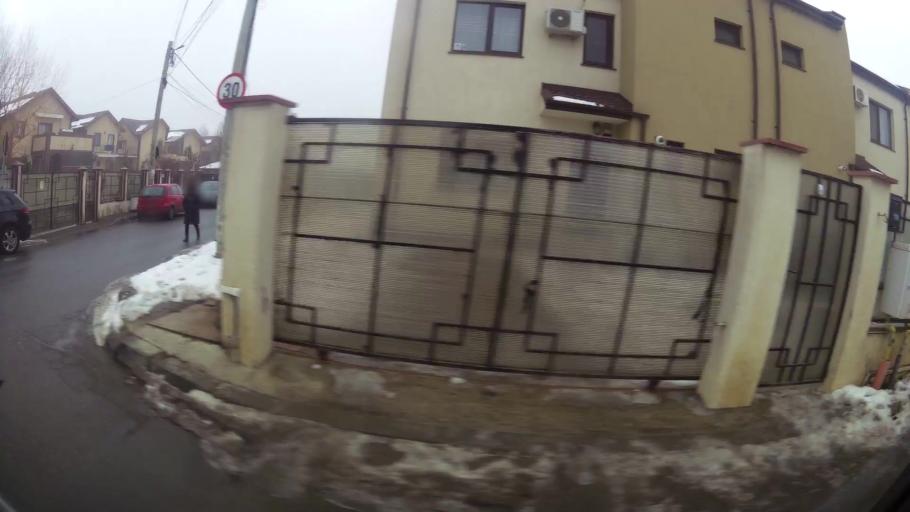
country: RO
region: Ilfov
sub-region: Comuna Chiajna
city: Chiajna
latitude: 44.4524
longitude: 25.9842
